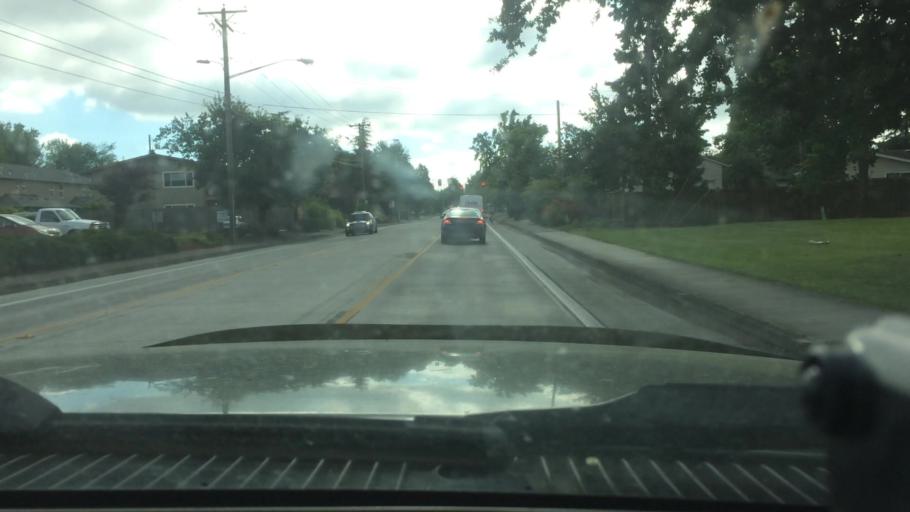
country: US
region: Oregon
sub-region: Lane County
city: Eugene
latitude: 44.0404
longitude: -123.1144
